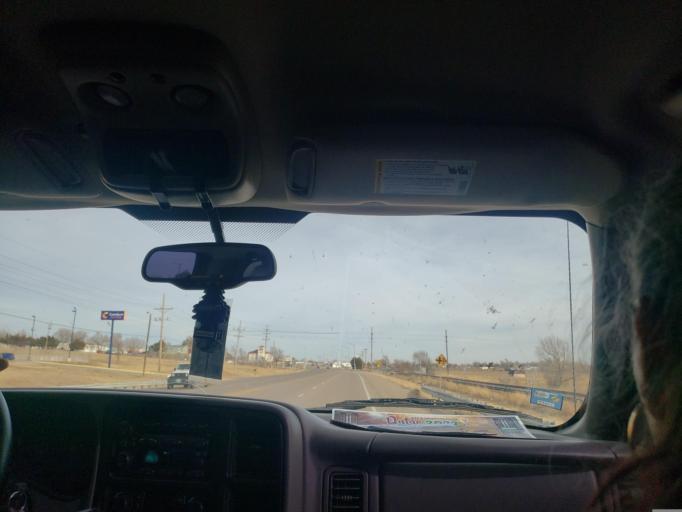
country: US
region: Kansas
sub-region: Ford County
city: Dodge City
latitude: 37.7547
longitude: -100.0537
